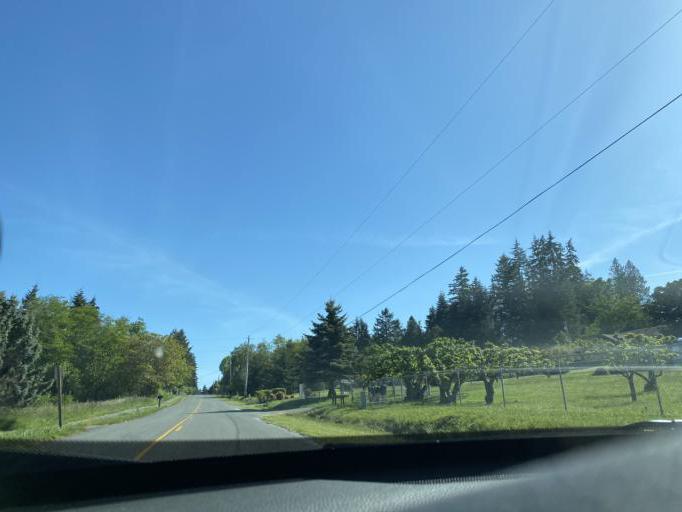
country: US
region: Washington
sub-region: Island County
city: Freeland
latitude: 48.0150
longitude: -122.5313
